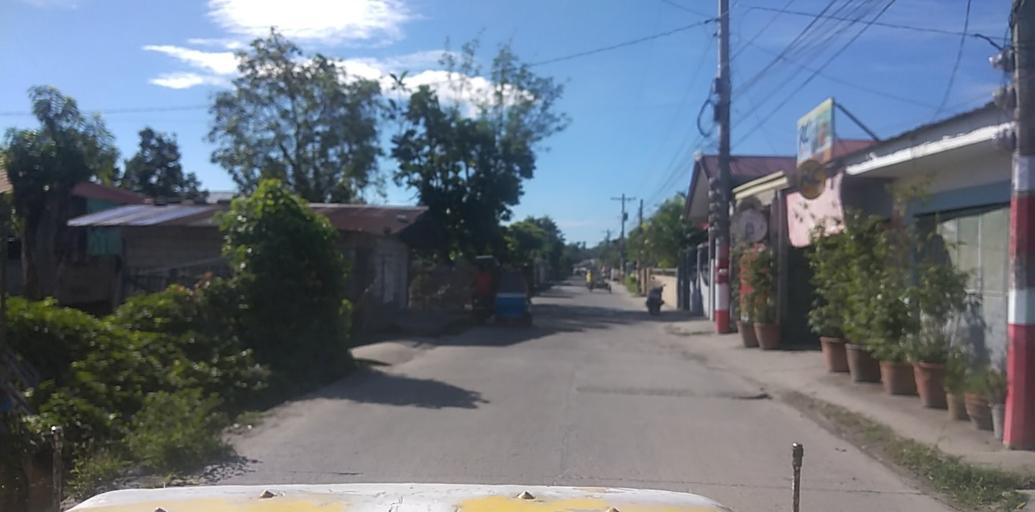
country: PH
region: Central Luzon
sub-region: Province of Pampanga
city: San Patricio
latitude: 15.1019
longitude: 120.7138
